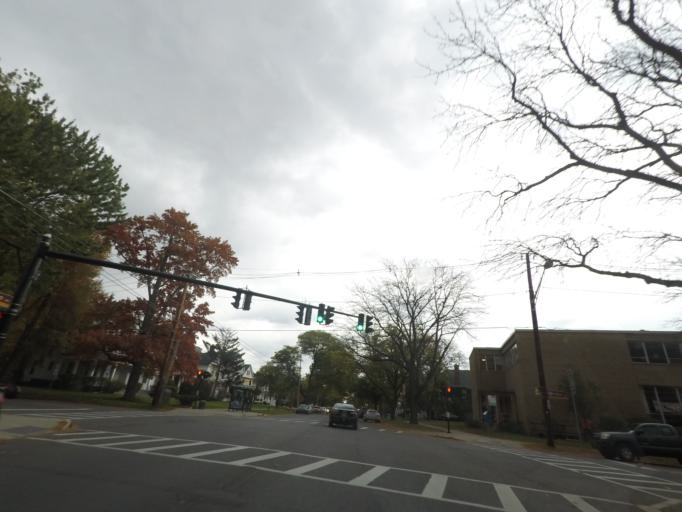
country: US
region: New York
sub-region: Albany County
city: West Albany
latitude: 42.6654
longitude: -73.7884
